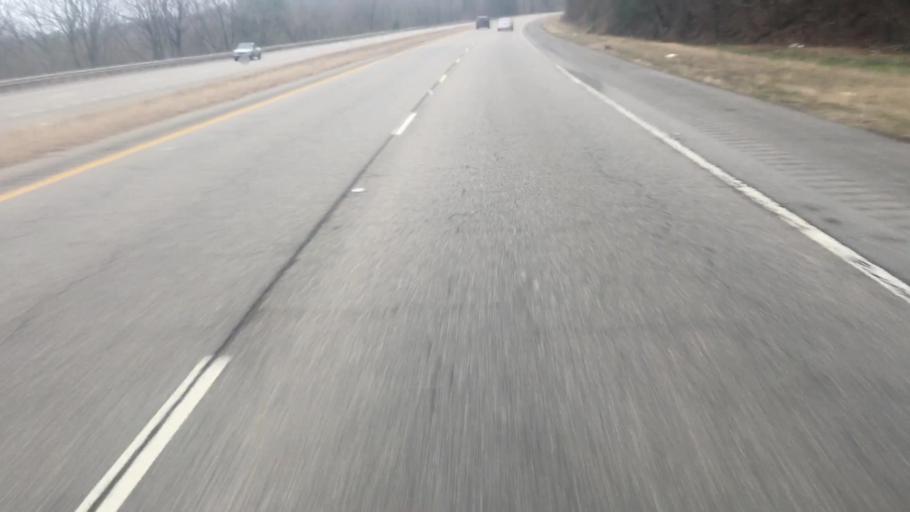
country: US
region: Alabama
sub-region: Walker County
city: Cordova
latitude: 33.8168
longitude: -87.1500
